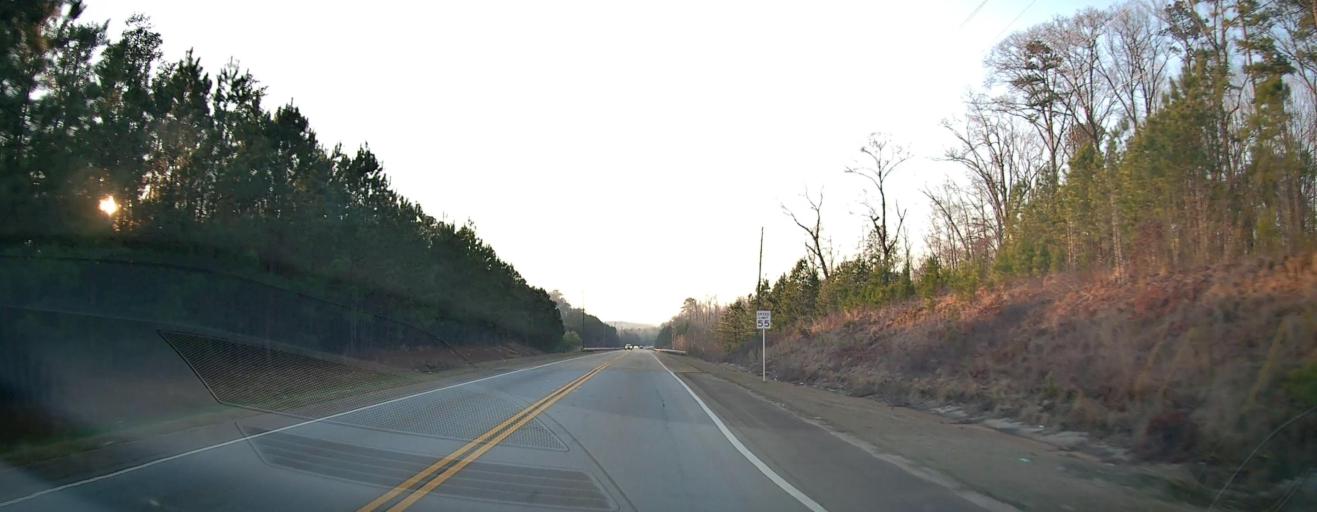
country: US
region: Georgia
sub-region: Troup County
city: La Grange
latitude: 32.9914
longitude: -85.0718
